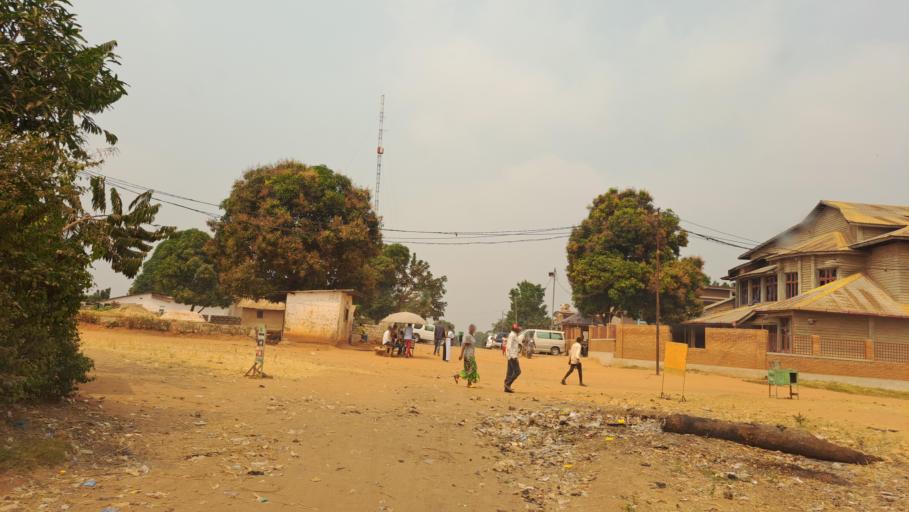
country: CD
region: Kasai-Oriental
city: Mbuji-Mayi
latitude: -6.1090
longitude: 23.5967
